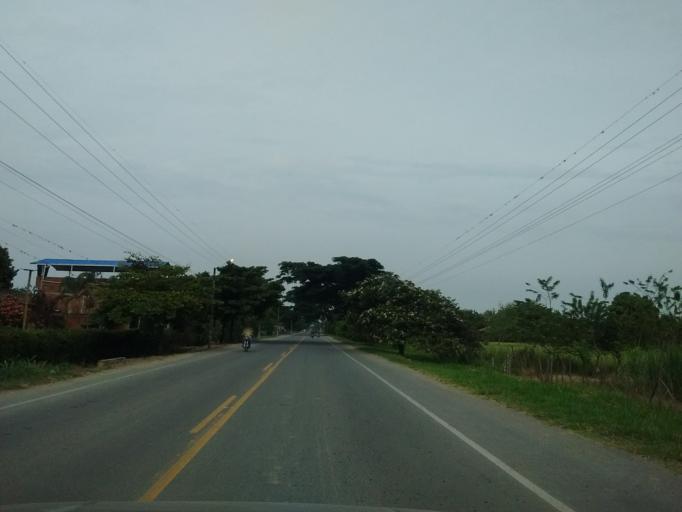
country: CO
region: Cauca
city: Puerto Tejada
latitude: 3.1823
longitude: -76.4521
